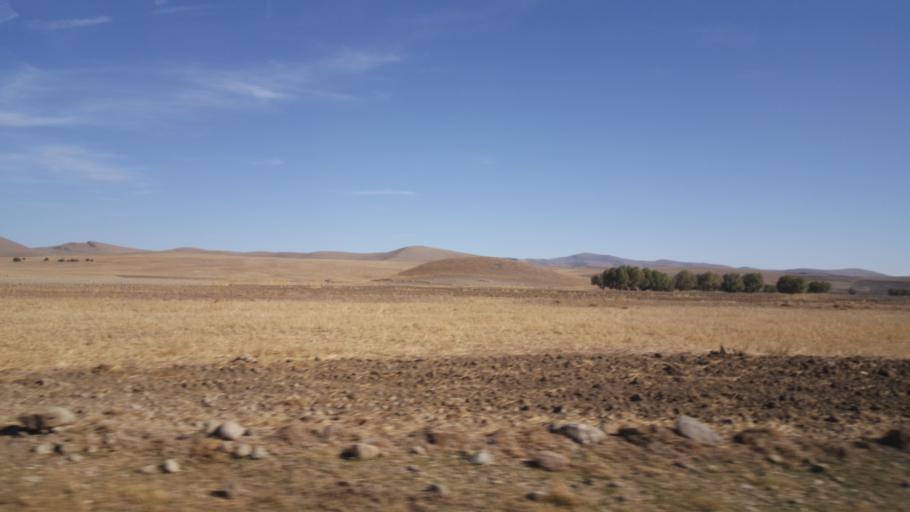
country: TR
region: Ankara
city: Altpinar
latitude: 39.2522
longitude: 32.7513
